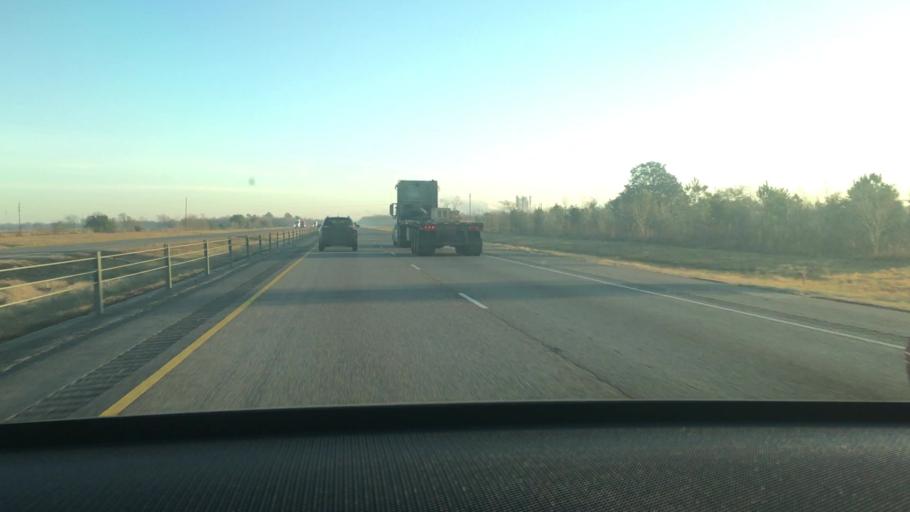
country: US
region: Texas
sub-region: Jefferson County
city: Fannett
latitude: 29.9618
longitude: -94.2341
